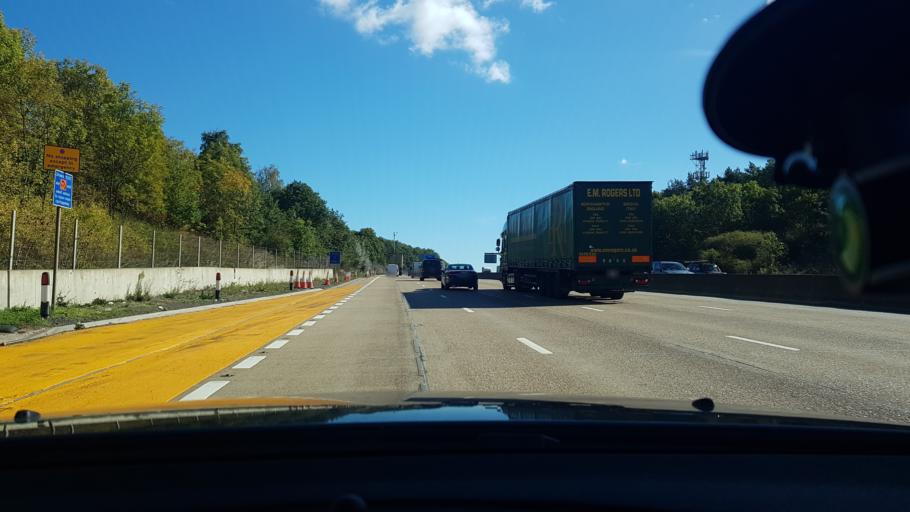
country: GB
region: England
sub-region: Hertfordshire
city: Cuffley
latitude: 51.6897
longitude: -0.0889
